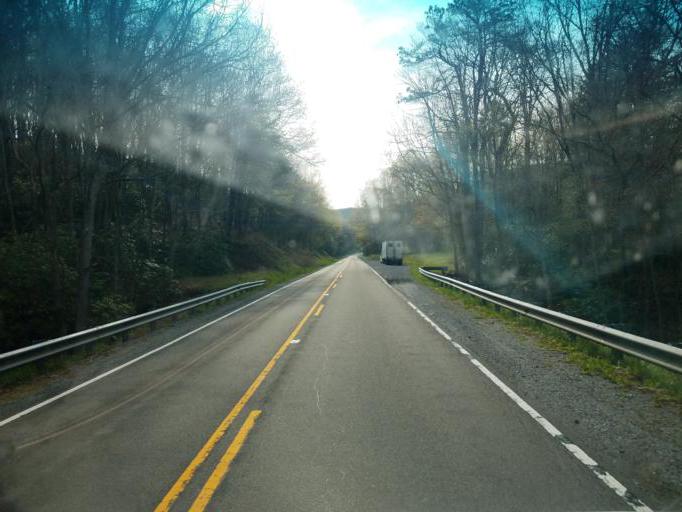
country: US
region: Virginia
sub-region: Smyth County
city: Atkins
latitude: 36.8109
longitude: -81.4137
